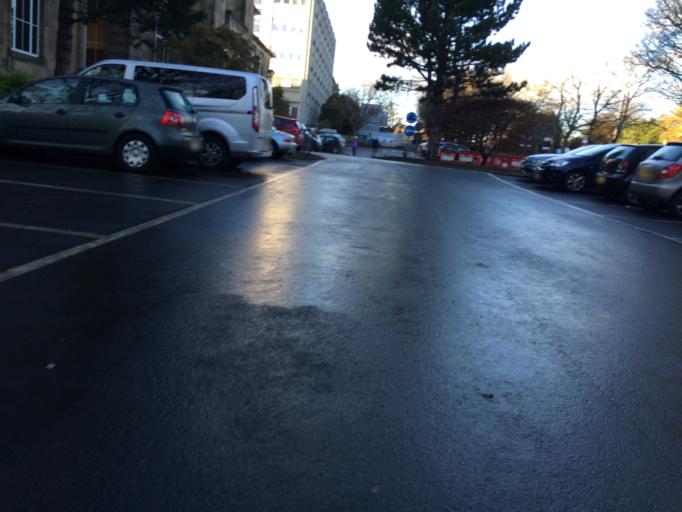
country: GB
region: Scotland
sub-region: Edinburgh
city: Edinburgh
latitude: 55.9229
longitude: -3.1712
